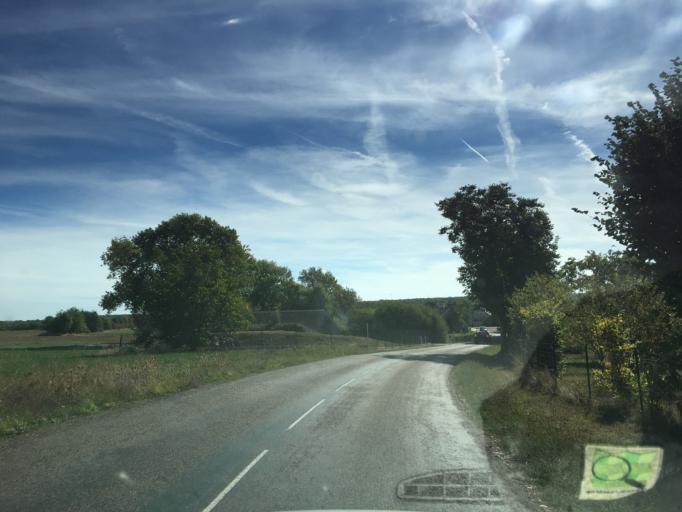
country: FR
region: Bourgogne
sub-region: Departement de l'Yonne
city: Vermenton
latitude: 47.5880
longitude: 3.7053
